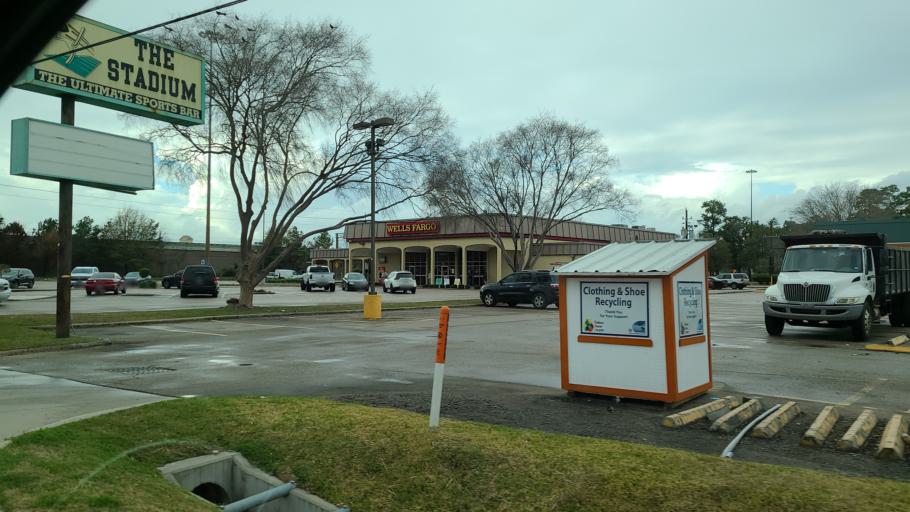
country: US
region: Texas
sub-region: Harris County
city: Spring
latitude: 30.0756
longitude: -95.4345
